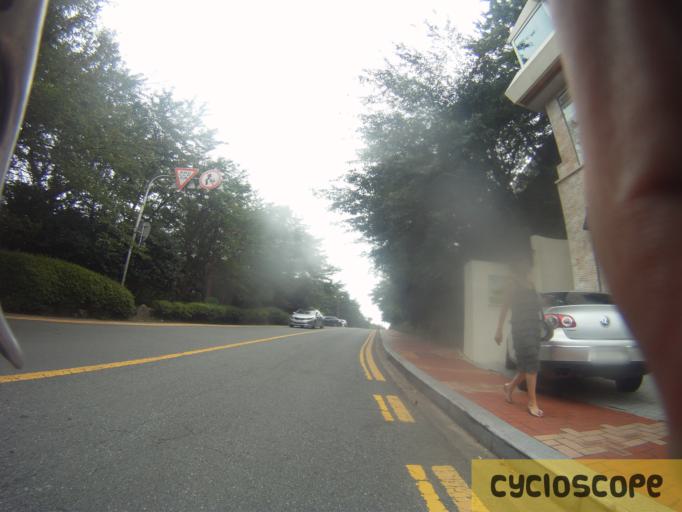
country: KR
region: Busan
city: Kijang
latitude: 35.1608
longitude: 129.1843
